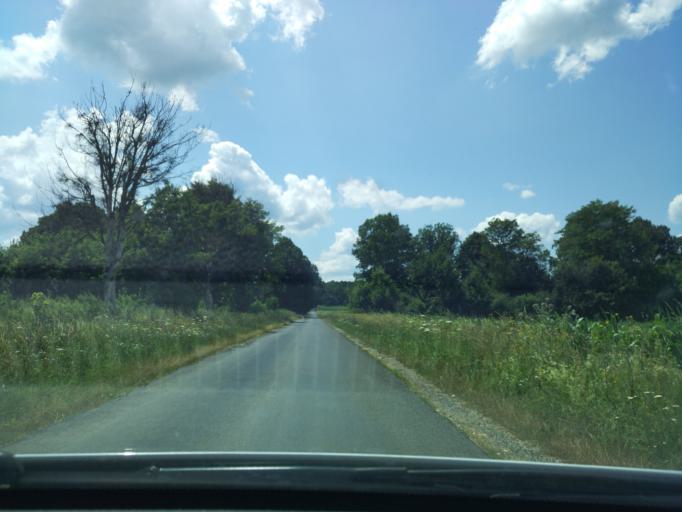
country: HU
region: Veszprem
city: Urkut
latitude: 47.0723
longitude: 17.6816
